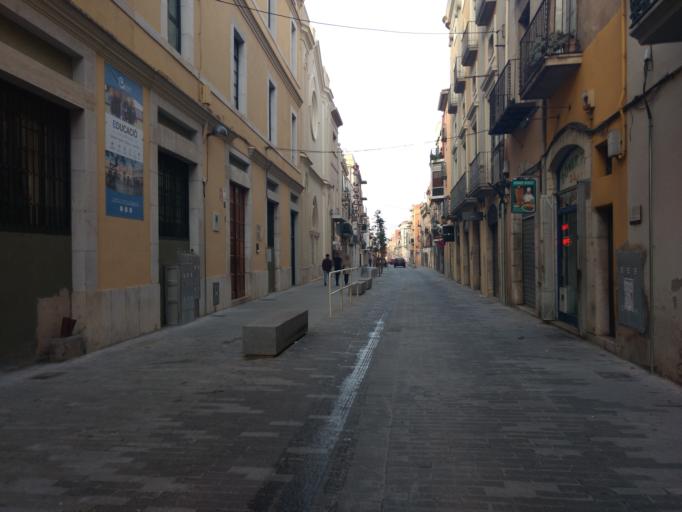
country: ES
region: Catalonia
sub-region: Provincia de Girona
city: Figueres
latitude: 42.2685
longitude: 2.9628
